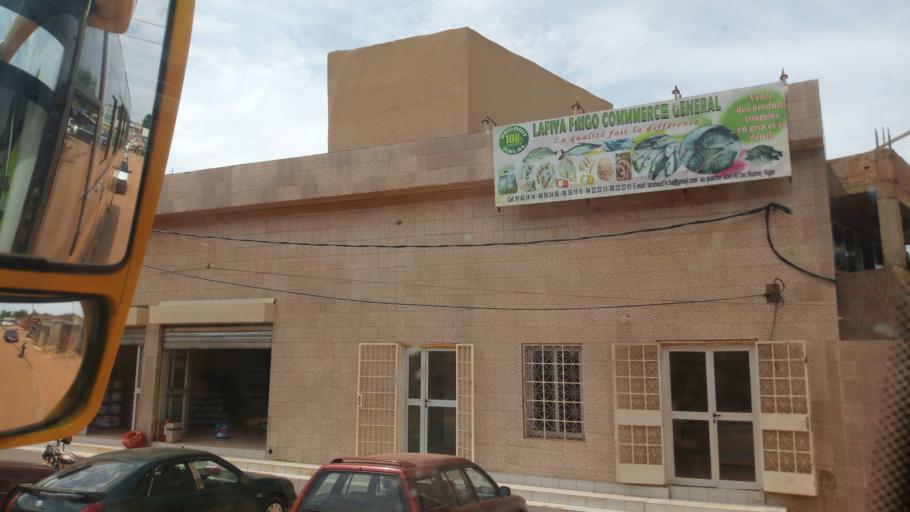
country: NE
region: Niamey
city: Niamey
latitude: 13.5193
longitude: 2.1236
